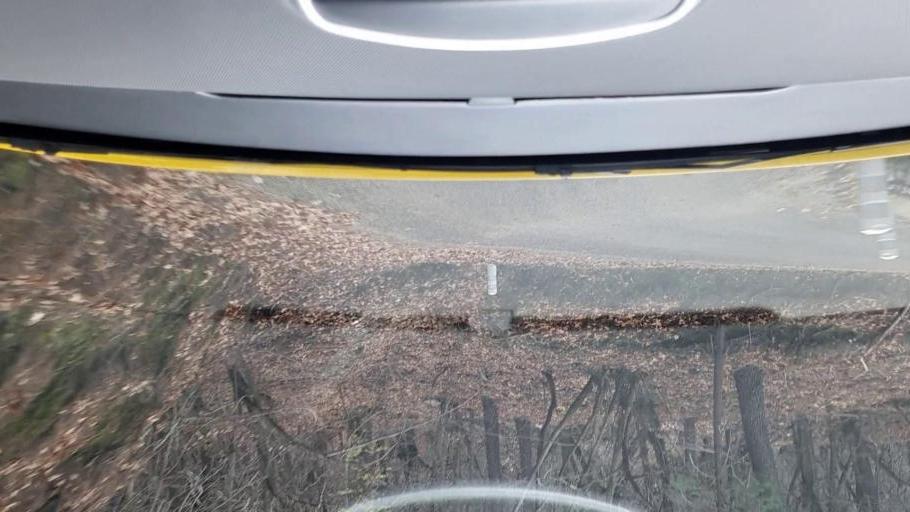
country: FR
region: Languedoc-Roussillon
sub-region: Departement du Gard
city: Branoux-les-Taillades
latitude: 44.2304
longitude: 3.9582
